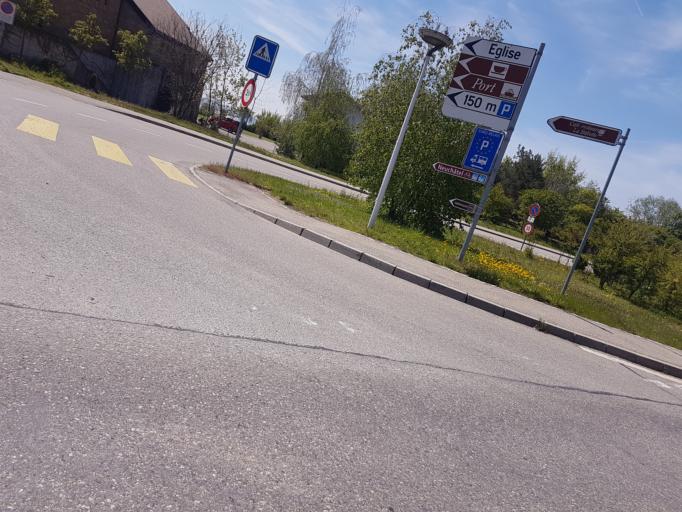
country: CH
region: Neuchatel
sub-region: Neuchatel District
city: Saint-Blaise
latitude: 47.0118
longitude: 6.9896
